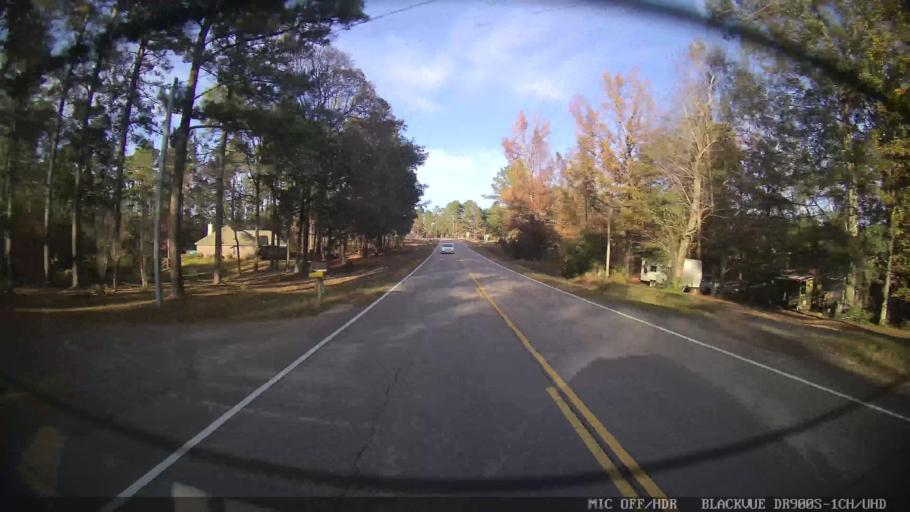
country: US
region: Mississippi
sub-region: Lamar County
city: Purvis
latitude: 31.1888
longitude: -89.2885
